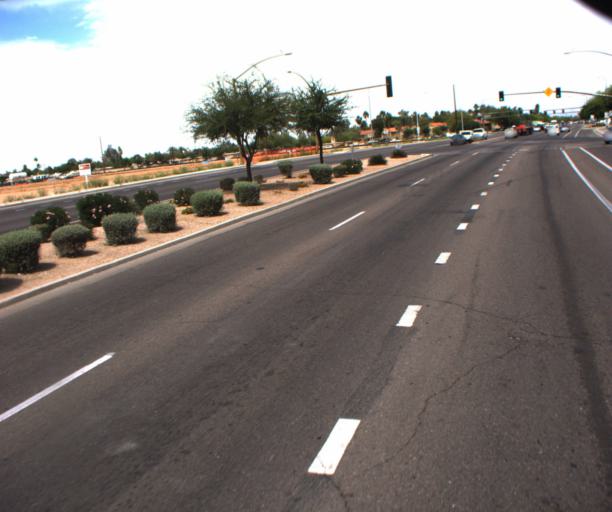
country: US
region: Arizona
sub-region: Maricopa County
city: Chandler
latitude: 33.2892
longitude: -111.8415
